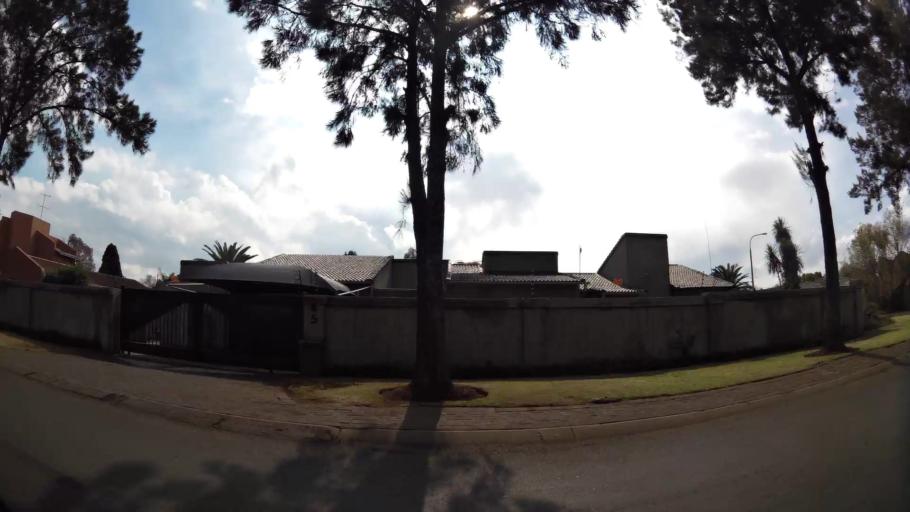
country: ZA
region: Gauteng
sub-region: Sedibeng District Municipality
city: Vanderbijlpark
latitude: -26.7384
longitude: 27.8453
